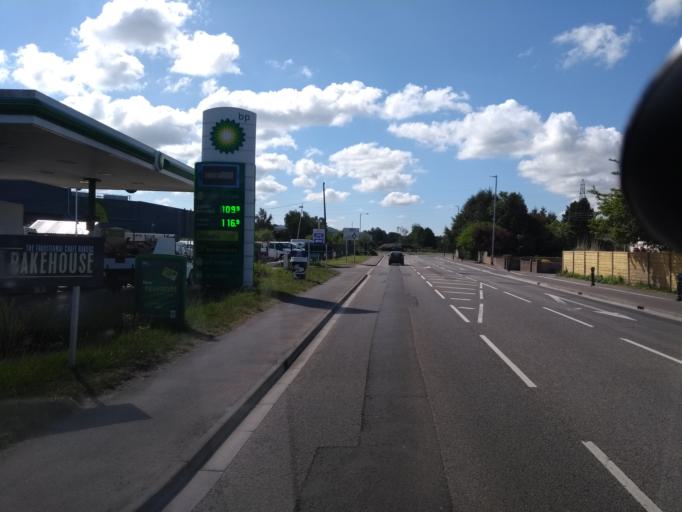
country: GB
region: England
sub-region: Somerset
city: Bridgwater
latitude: 51.1138
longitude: -2.9957
